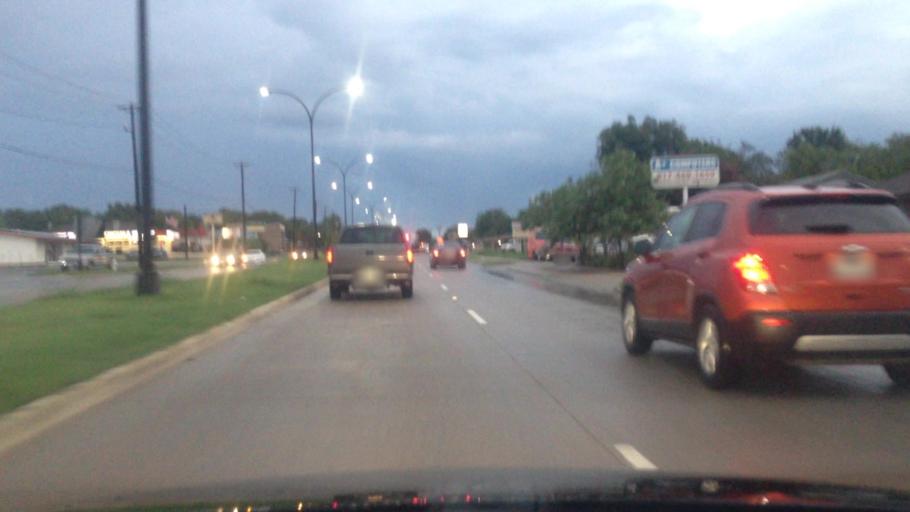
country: US
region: Texas
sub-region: Tarrant County
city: Arlington
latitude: 32.7354
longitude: -97.0834
